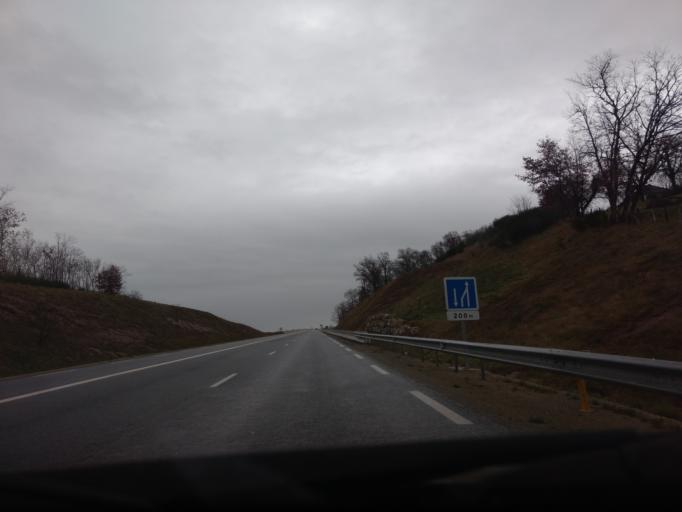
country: FR
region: Midi-Pyrenees
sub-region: Departement de l'Aveyron
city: Firmi
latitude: 44.5161
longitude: 2.3501
